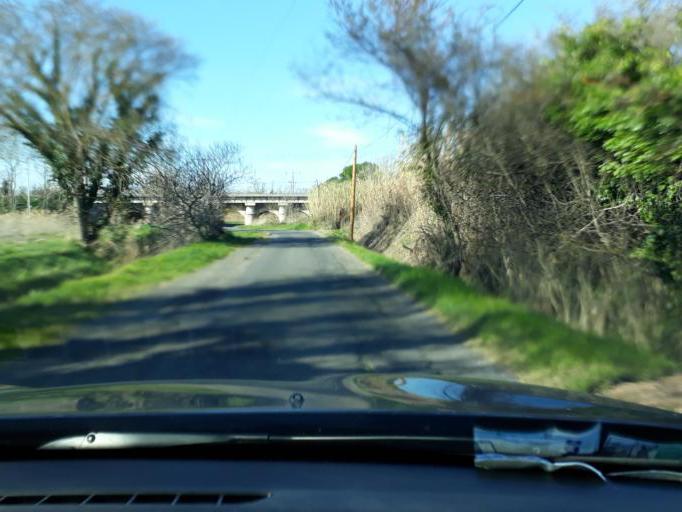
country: FR
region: Languedoc-Roussillon
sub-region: Departement de l'Herault
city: Agde
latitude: 43.3155
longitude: 3.4588
